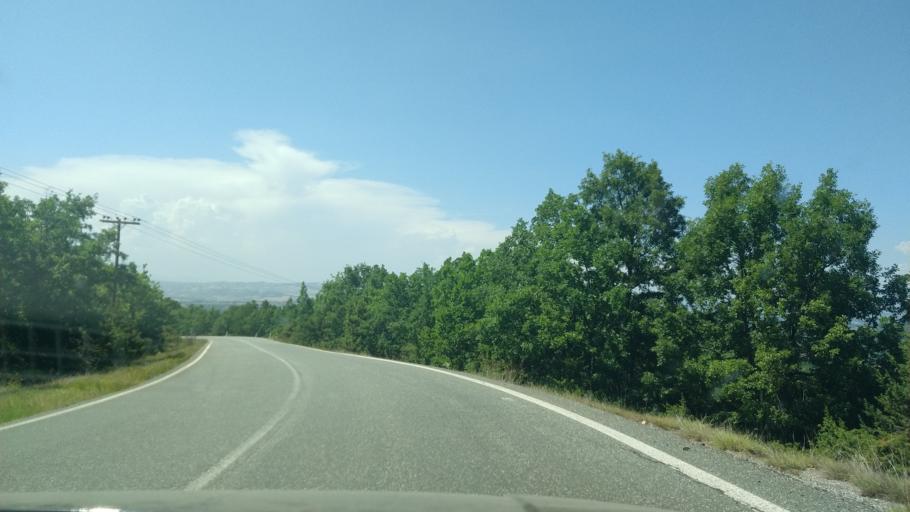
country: GR
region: West Macedonia
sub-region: Nomos Grevenon
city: Grevena
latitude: 40.0201
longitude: 21.4875
